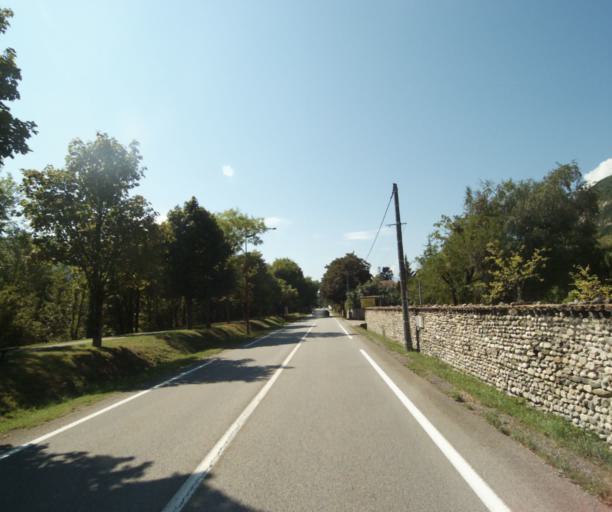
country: FR
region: Rhone-Alpes
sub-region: Departement de l'Isere
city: Vif
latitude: 45.0588
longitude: 5.6681
